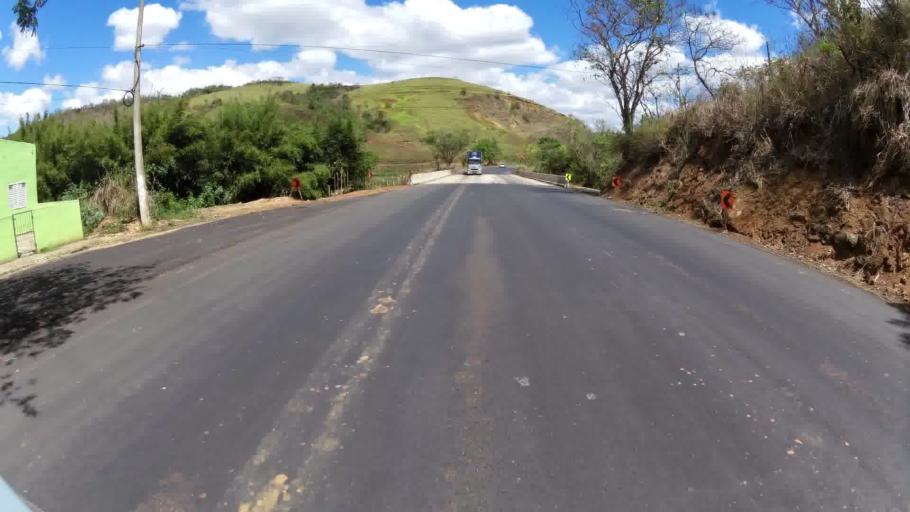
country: BR
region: Rio de Janeiro
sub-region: Itaperuna
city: Itaperuna
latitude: -21.3611
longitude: -41.9258
